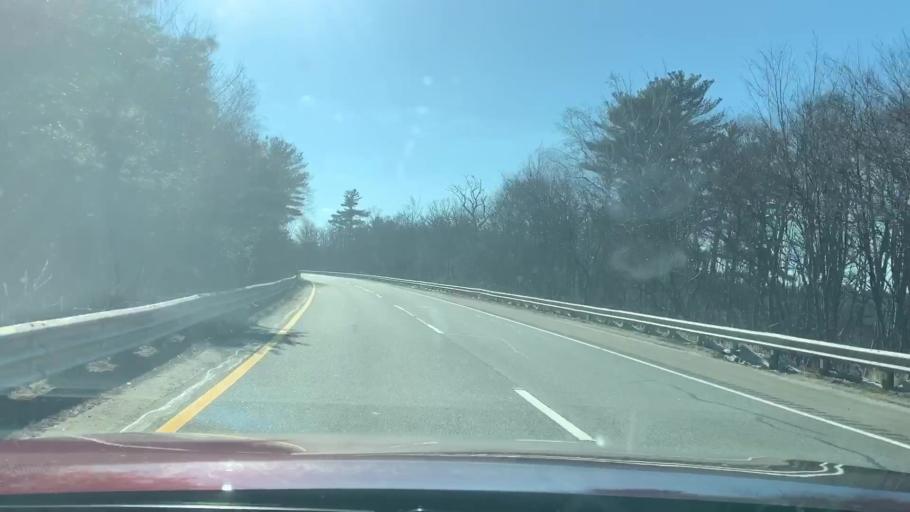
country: US
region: Massachusetts
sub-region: Essex County
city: Essex
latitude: 42.6123
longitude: -70.7339
